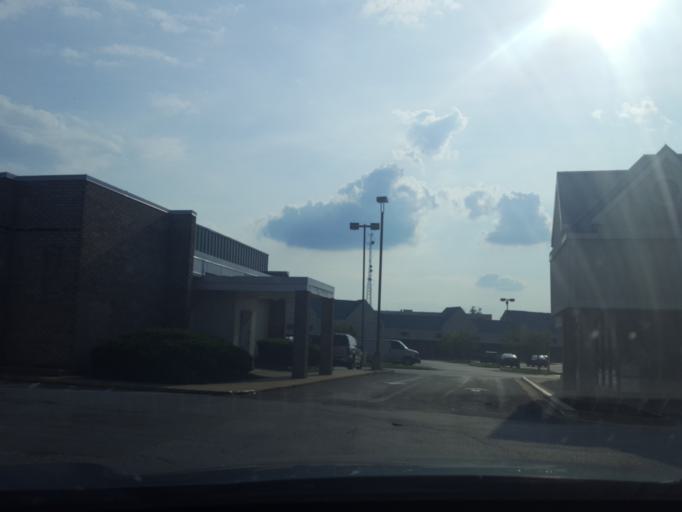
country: US
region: Maryland
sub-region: Prince George's County
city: Oxon Hill
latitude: 38.8044
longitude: -76.9905
